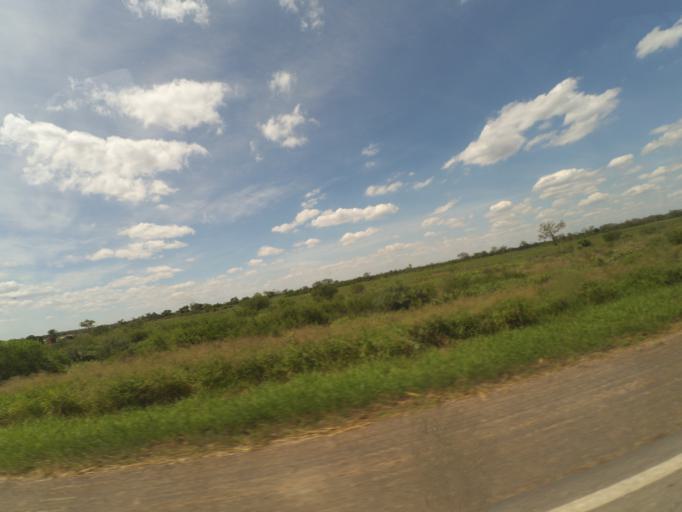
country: BO
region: Santa Cruz
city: Pailon
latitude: -17.5892
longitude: -61.9519
